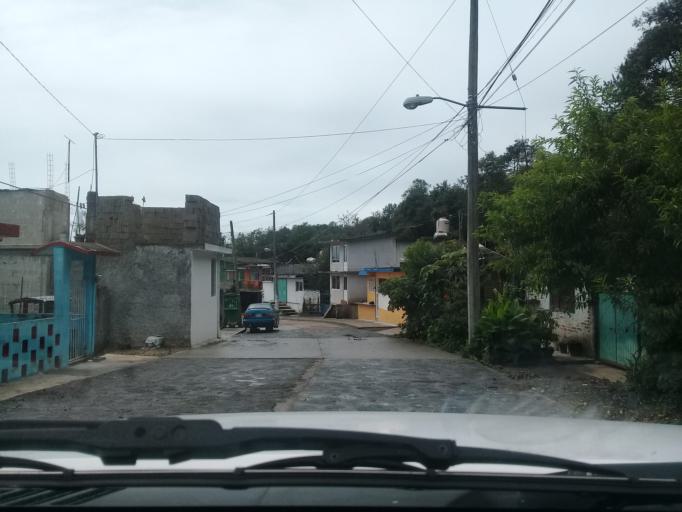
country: MX
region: Veracruz
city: Rafael Lucio
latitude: 19.5901
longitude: -96.9933
